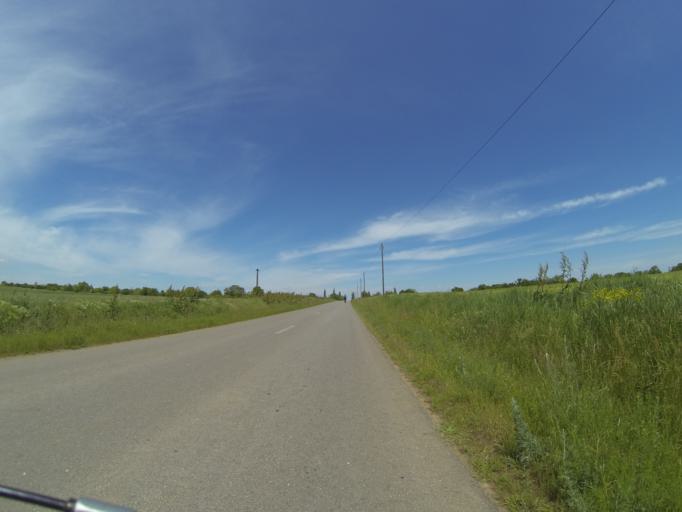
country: RO
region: Dolj
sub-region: Comuna Diosti
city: Radomir
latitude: 44.1523
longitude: 24.1634
